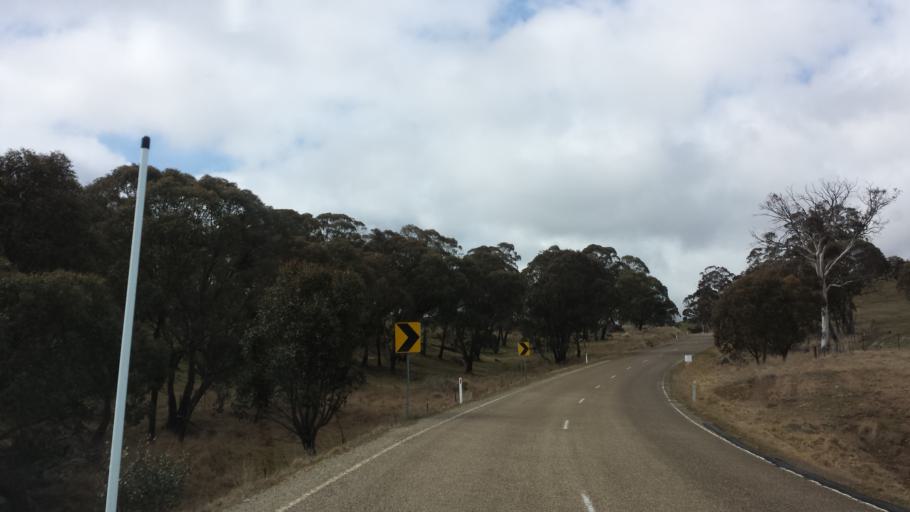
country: AU
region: Victoria
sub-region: Alpine
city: Mount Beauty
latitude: -37.0951
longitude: 147.4075
